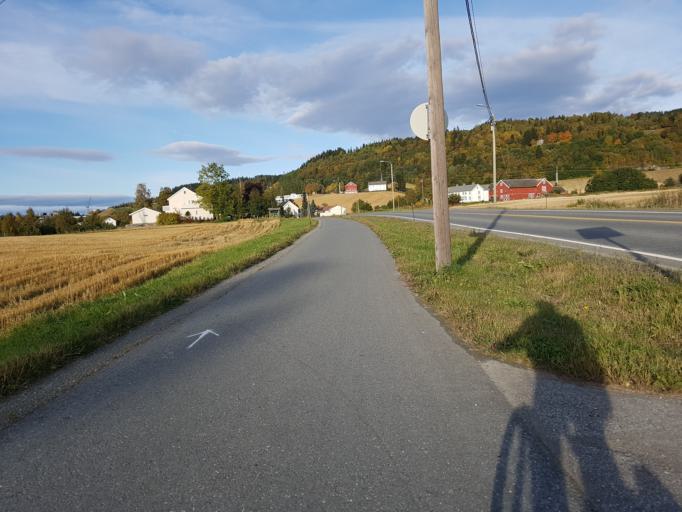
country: NO
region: Sor-Trondelag
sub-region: Trondheim
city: Trondheim
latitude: 63.3774
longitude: 10.4324
